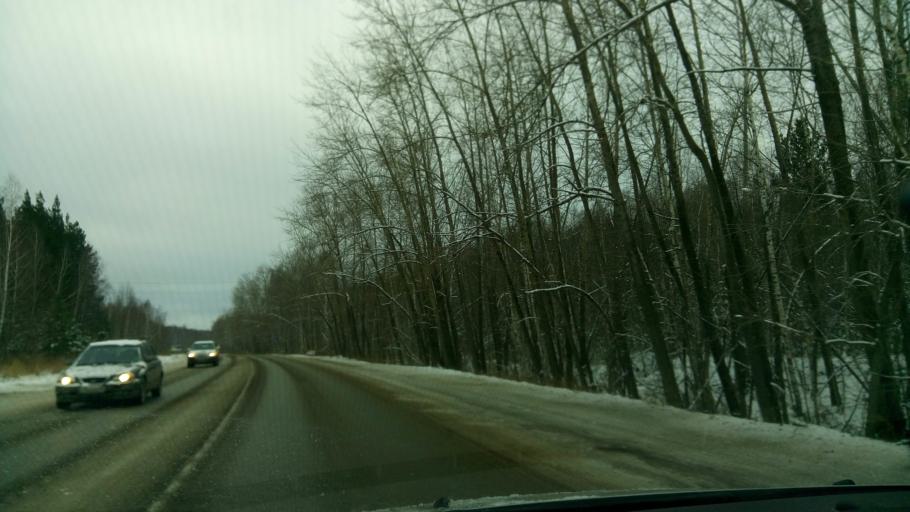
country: RU
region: Sverdlovsk
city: Polevskoy
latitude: 56.4685
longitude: 60.2272
